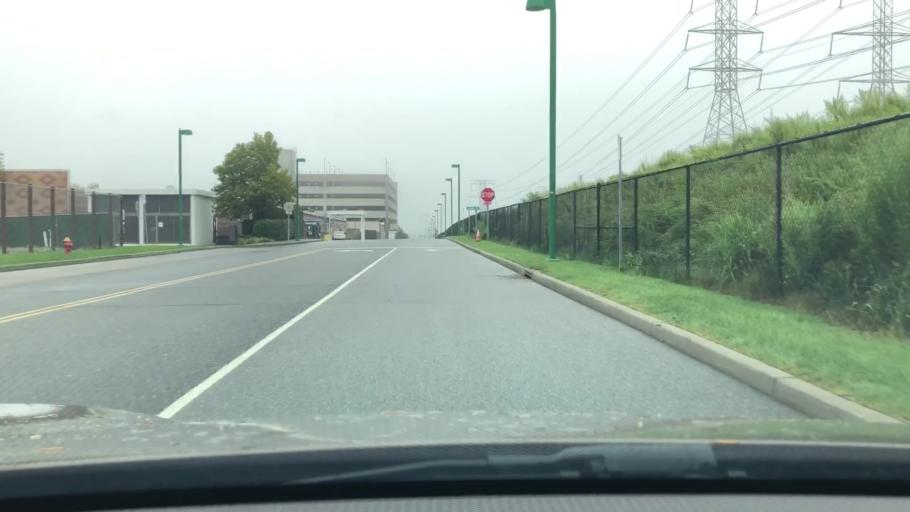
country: US
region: New York
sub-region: Westchester County
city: Tuckahoe
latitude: 40.9605
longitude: -73.8555
